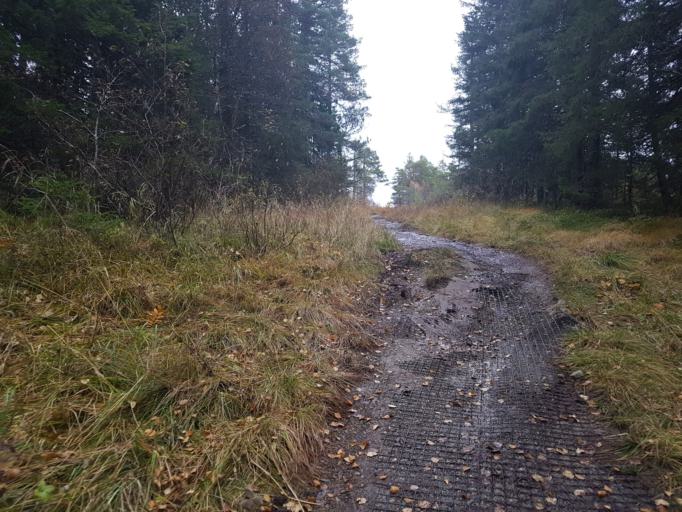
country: NO
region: Sor-Trondelag
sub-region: Melhus
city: Melhus
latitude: 63.3849
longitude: 10.2425
